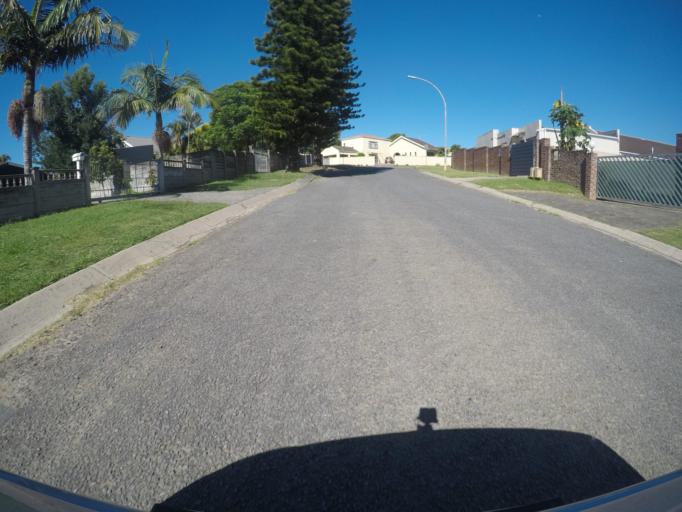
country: ZA
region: Eastern Cape
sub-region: Buffalo City Metropolitan Municipality
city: East London
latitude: -32.9467
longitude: 27.9021
